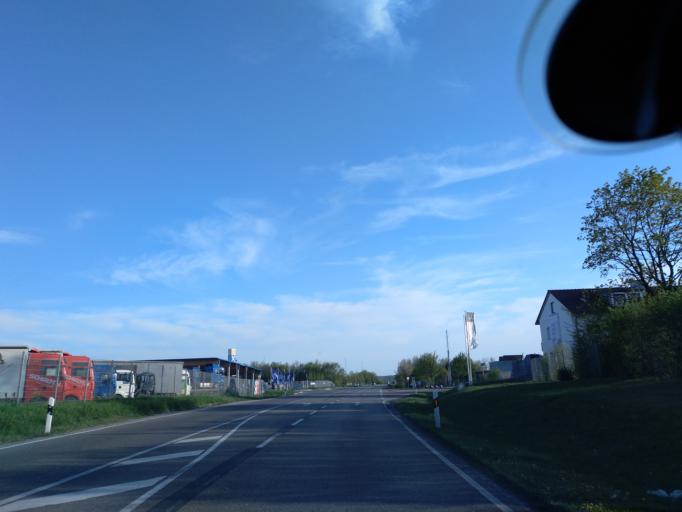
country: DE
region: Baden-Wuerttemberg
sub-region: Regierungsbezirk Stuttgart
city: Kirchberg an der Jagst
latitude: 49.1743
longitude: 9.9603
